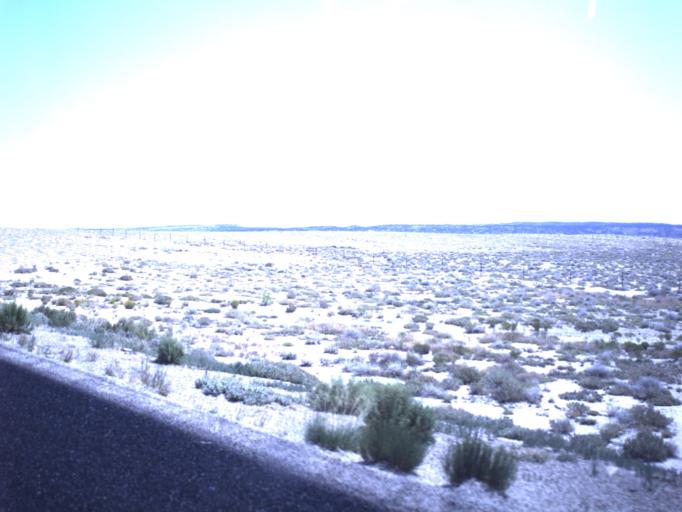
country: US
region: Utah
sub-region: Emery County
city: Ferron
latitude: 38.9703
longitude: -111.1832
